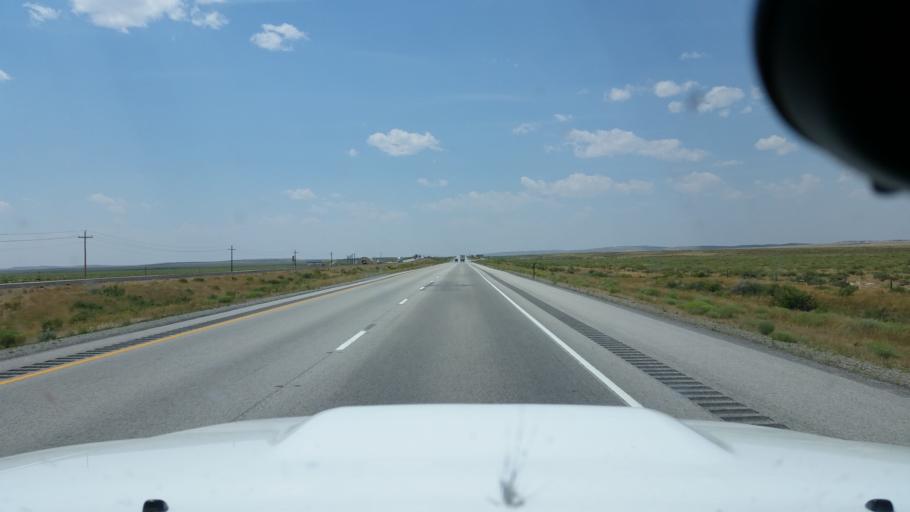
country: US
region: Wyoming
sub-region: Carbon County
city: Rawlins
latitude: 41.7755
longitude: -107.4564
